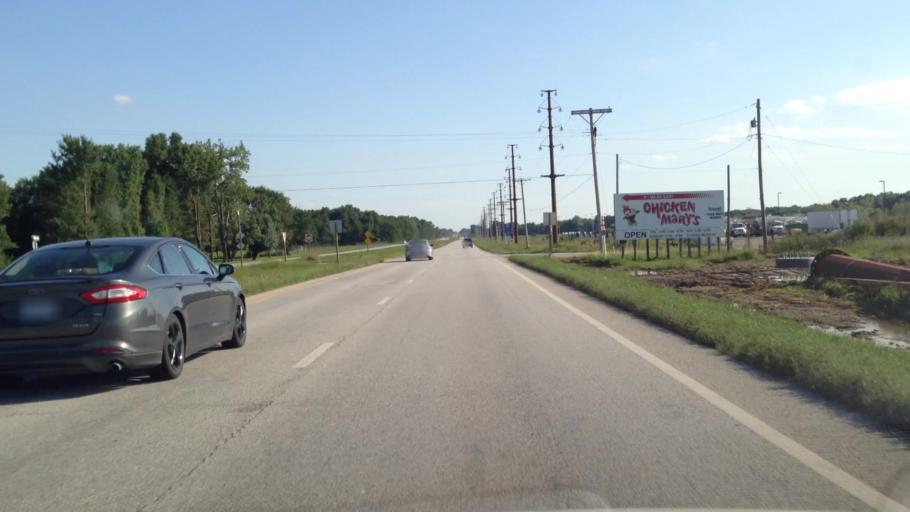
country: US
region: Kansas
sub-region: Crawford County
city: Frontenac
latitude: 37.4849
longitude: -94.7053
